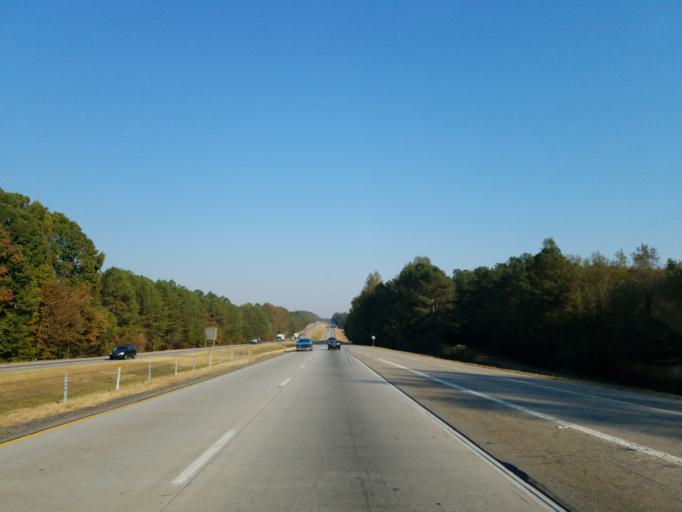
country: US
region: Georgia
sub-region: Bibb County
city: West Point
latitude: 32.9398
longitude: -83.7761
